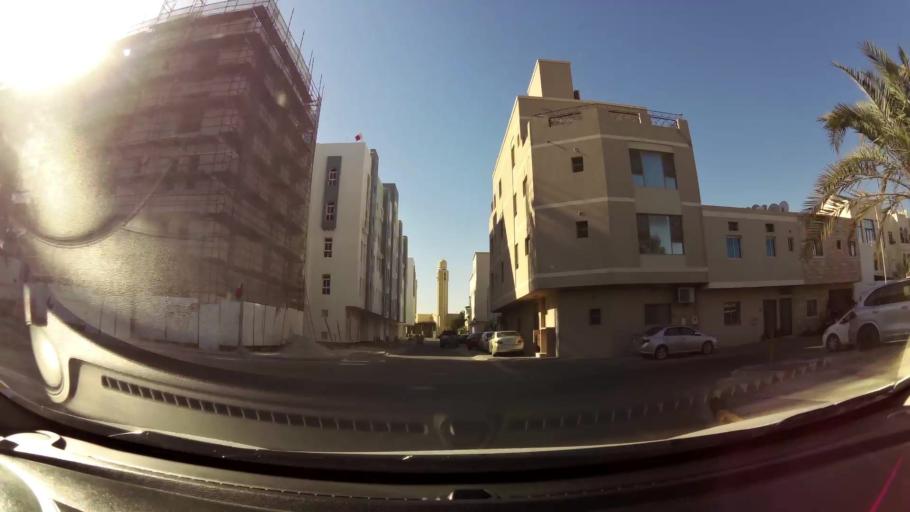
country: BH
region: Muharraq
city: Al Muharraq
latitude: 26.2602
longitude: 50.6056
